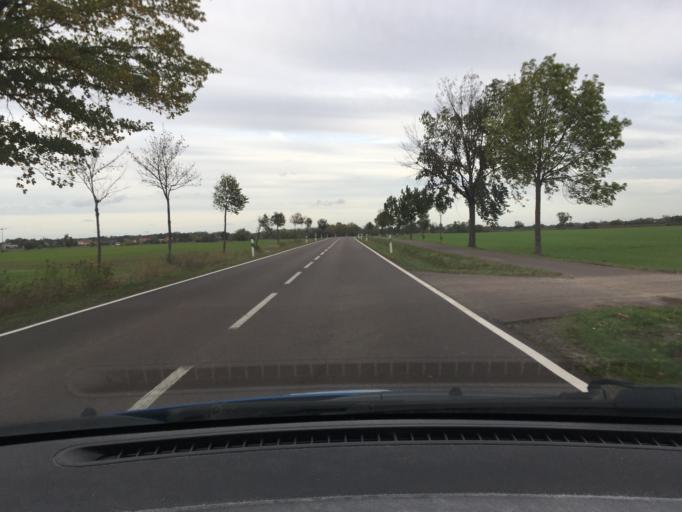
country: DE
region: Saxony-Anhalt
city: Wahlitz
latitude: 52.1216
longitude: 11.7632
